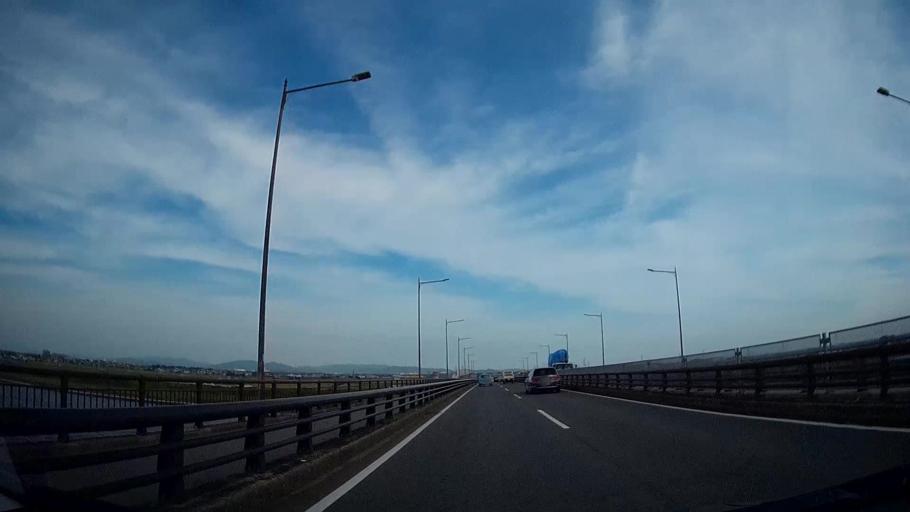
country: JP
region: Aichi
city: Hekinan
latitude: 34.8574
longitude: 136.9959
